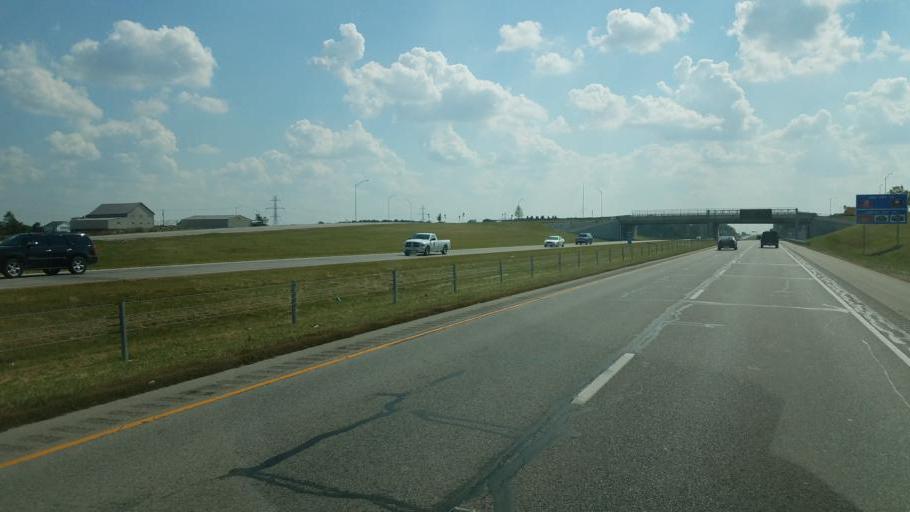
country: US
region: Indiana
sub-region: Allen County
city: Huntertown
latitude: 41.2024
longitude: -85.1045
